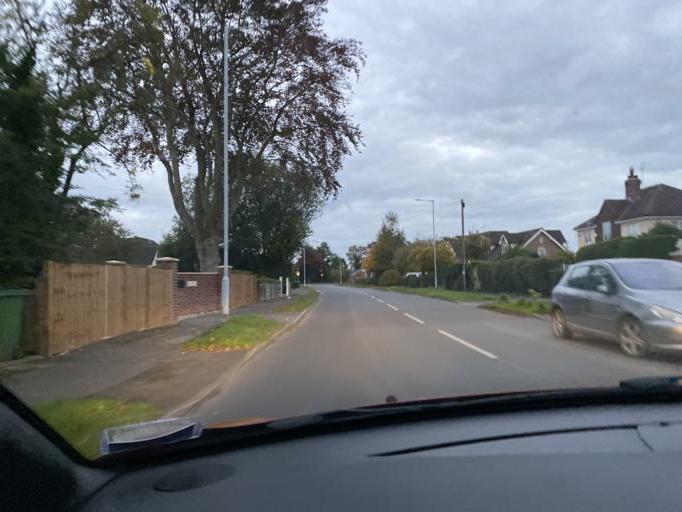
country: GB
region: England
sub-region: Borough of Stockport
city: Hazel Grove
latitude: 53.3675
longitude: -2.1246
